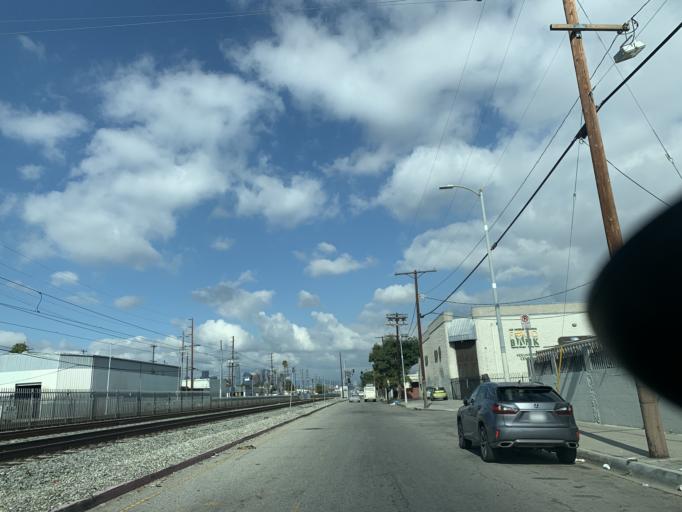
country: US
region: California
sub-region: Los Angeles County
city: Huntington Park
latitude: 34.0067
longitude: -118.2430
